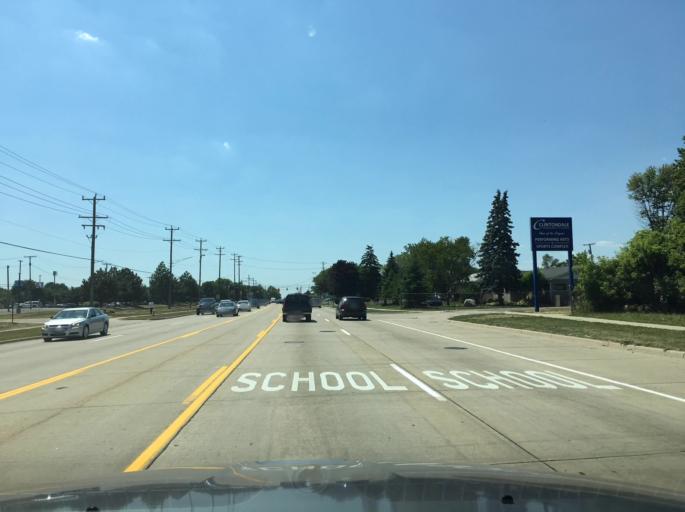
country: US
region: Michigan
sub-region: Macomb County
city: Clinton
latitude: 42.5545
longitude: -82.9070
